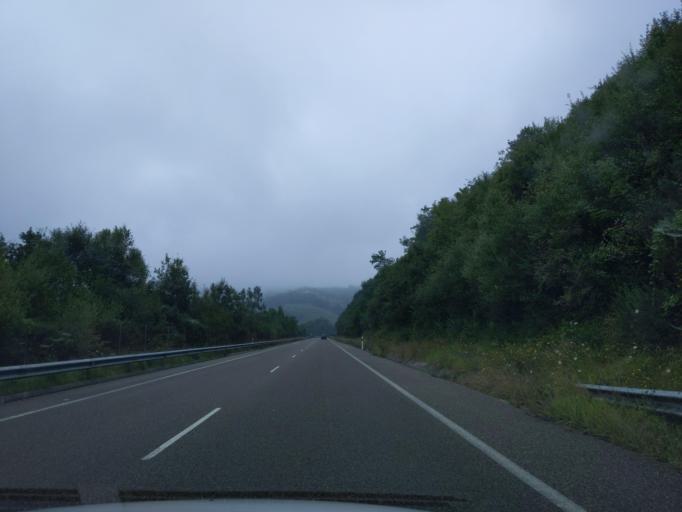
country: ES
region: Asturias
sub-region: Province of Asturias
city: El entrego
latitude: 43.3151
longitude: -5.5989
